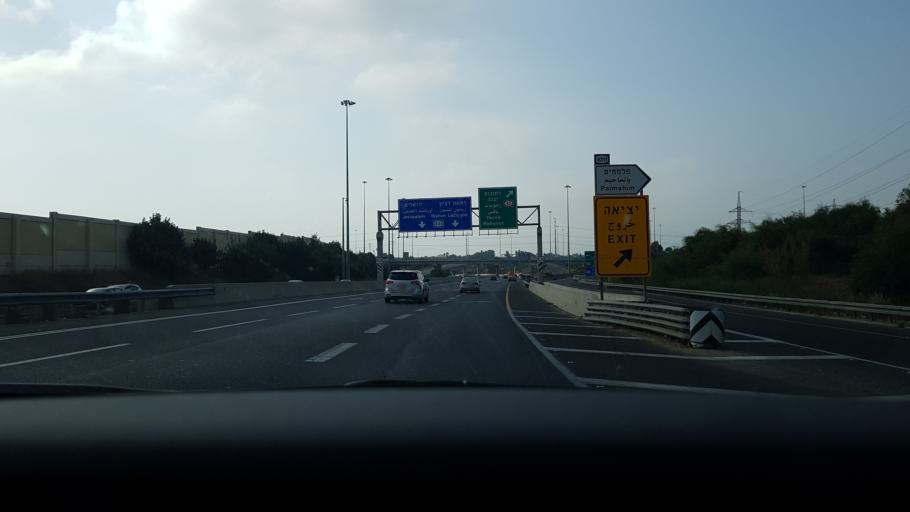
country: IL
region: Central District
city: Rishon LeZiyyon
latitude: 31.9600
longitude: 34.7854
